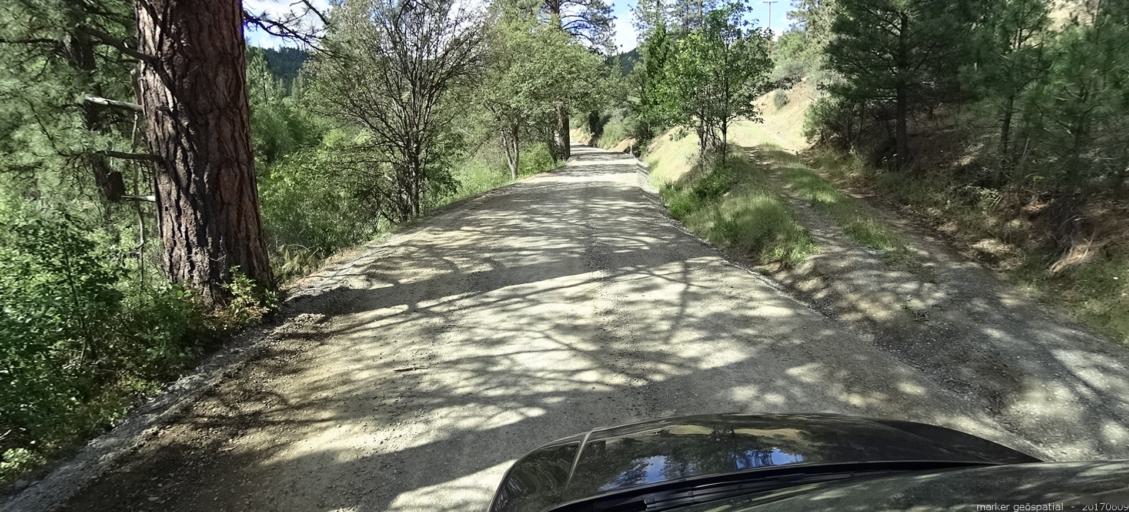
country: US
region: California
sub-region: Siskiyou County
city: Weed
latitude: 41.3139
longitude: -122.8202
